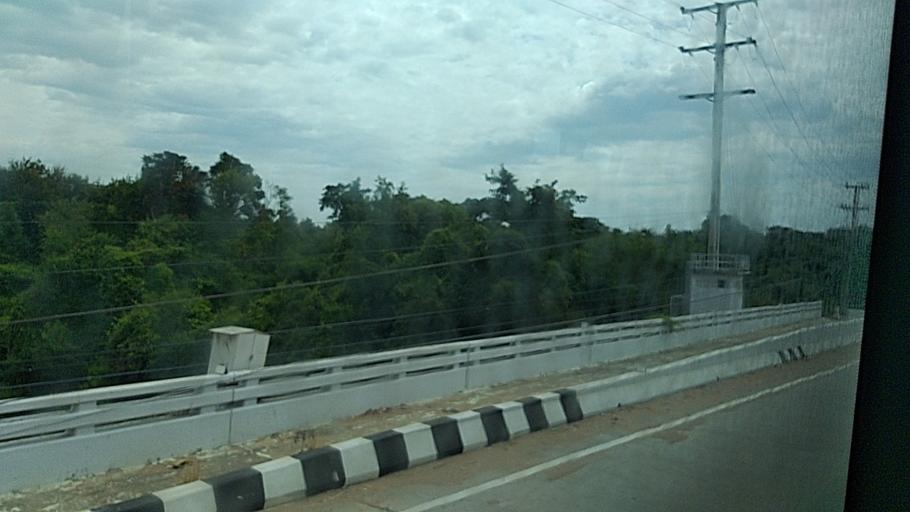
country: TH
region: Maha Sarakham
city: Maha Sarakham
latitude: 16.2320
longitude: 103.2710
